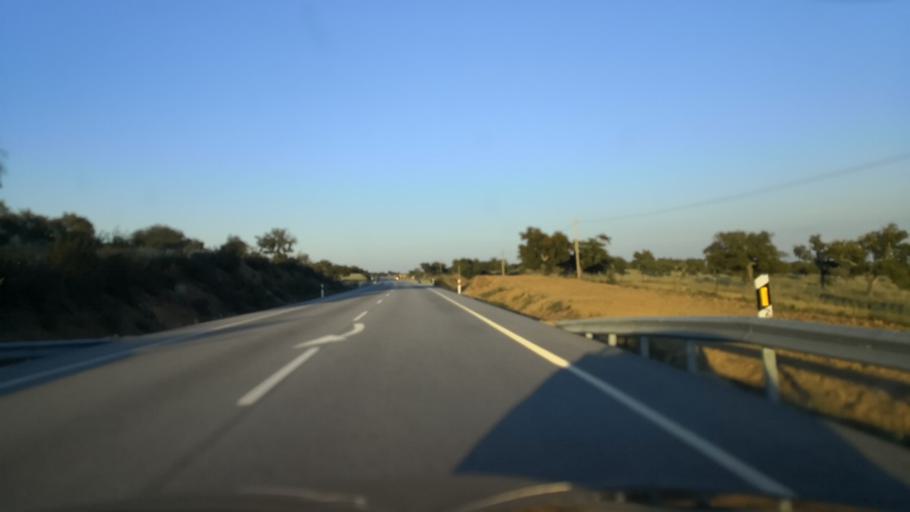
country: ES
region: Extremadura
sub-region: Provincia de Caceres
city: Carbajo
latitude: 39.5071
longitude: -7.1280
